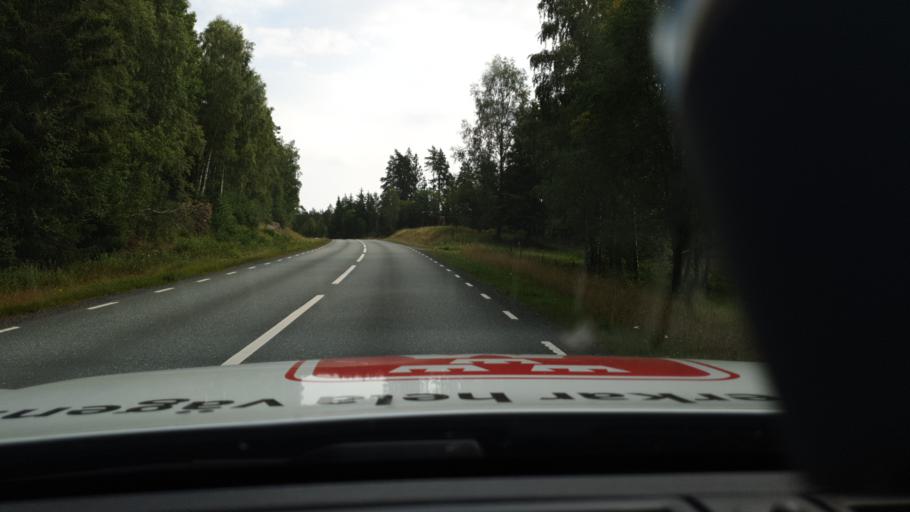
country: SE
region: Joenkoeping
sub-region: Nassjo Kommun
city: Nassjo
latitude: 57.7839
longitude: 14.6460
